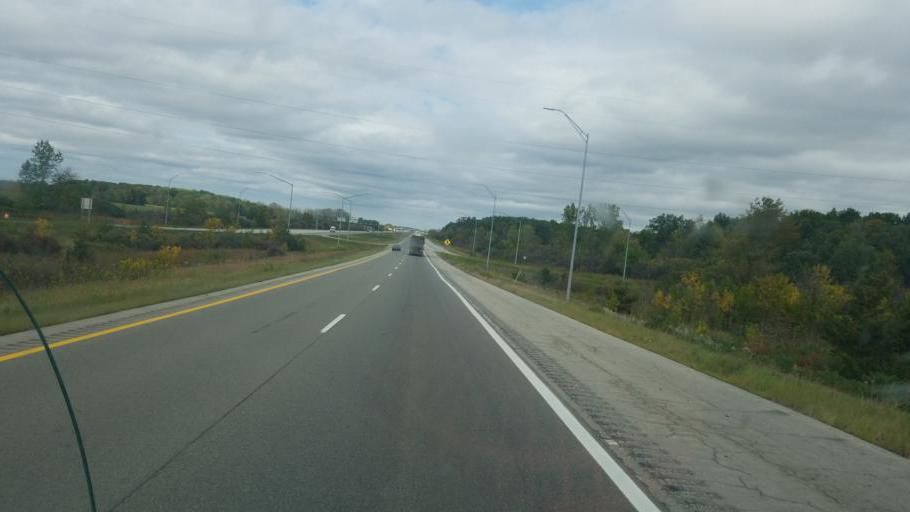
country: US
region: Michigan
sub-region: Monroe County
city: Woodland Beach
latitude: 41.9940
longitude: -83.3278
